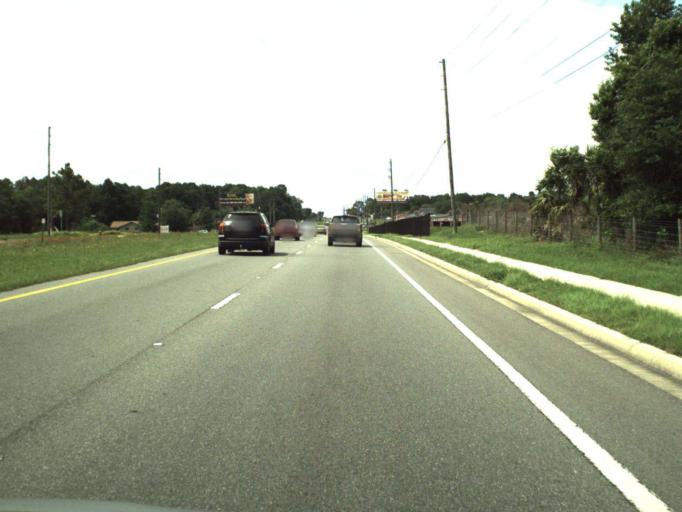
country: US
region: Florida
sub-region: Marion County
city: Silver Springs Shores
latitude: 29.1456
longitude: -82.0535
